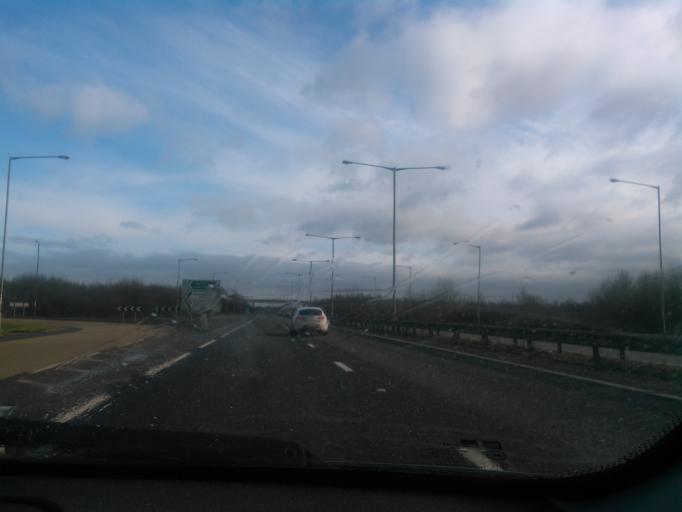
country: GB
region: England
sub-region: Derbyshire
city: Rodsley
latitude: 52.8817
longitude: -1.7078
